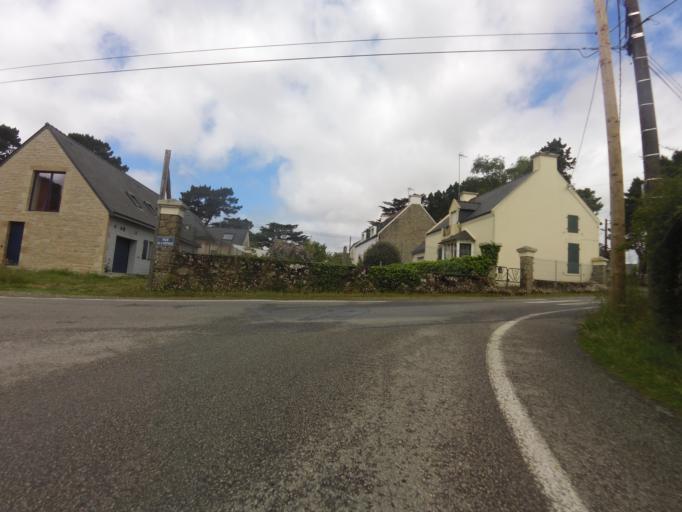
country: FR
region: Brittany
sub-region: Departement du Morbihan
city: Larmor-Baden
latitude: 47.5860
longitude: -2.8929
